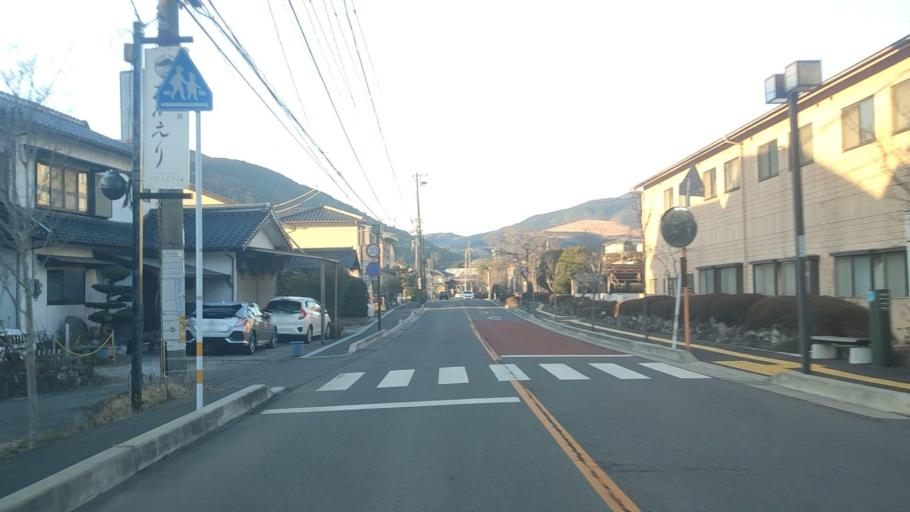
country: JP
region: Oita
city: Beppu
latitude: 33.2583
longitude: 131.3568
